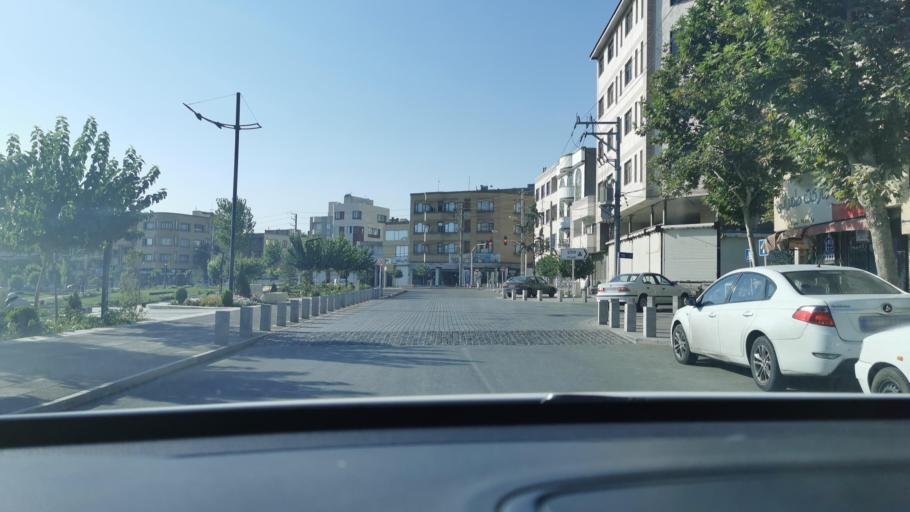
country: IR
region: Razavi Khorasan
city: Mashhad
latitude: 36.3104
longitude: 59.5110
